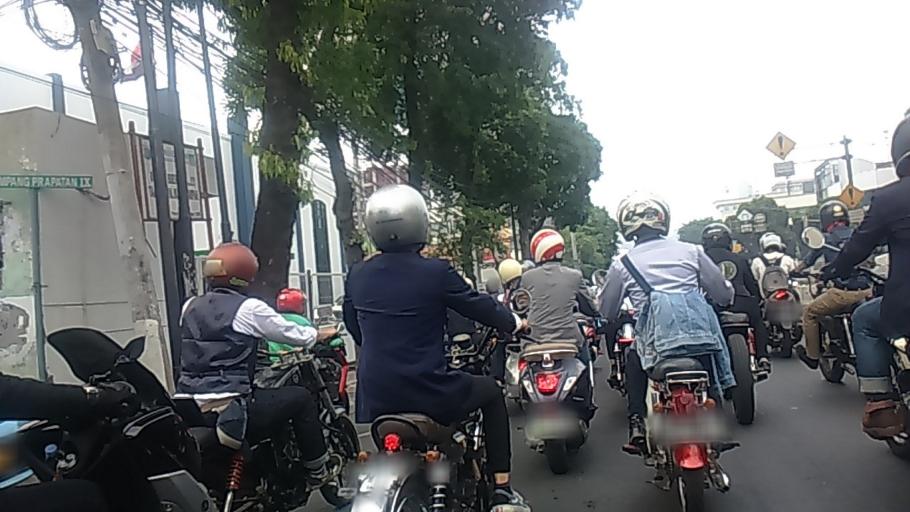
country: ID
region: Jakarta Raya
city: Jakarta
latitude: -6.2489
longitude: 106.8265
